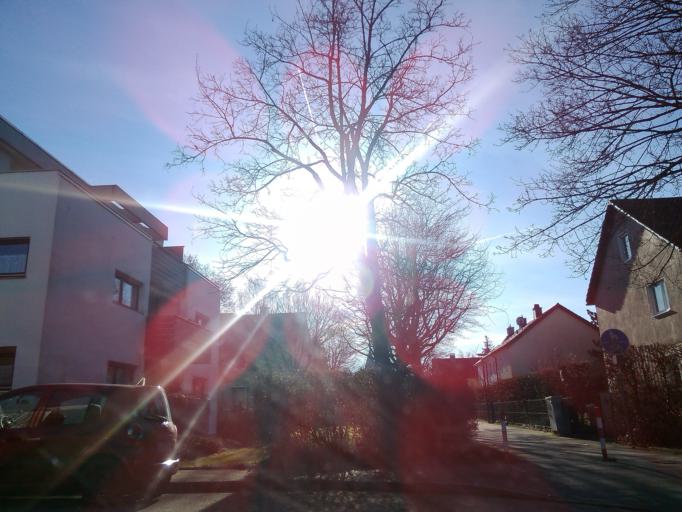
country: DE
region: Bavaria
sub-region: Upper Bavaria
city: Pasing
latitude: 48.1554
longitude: 11.4728
